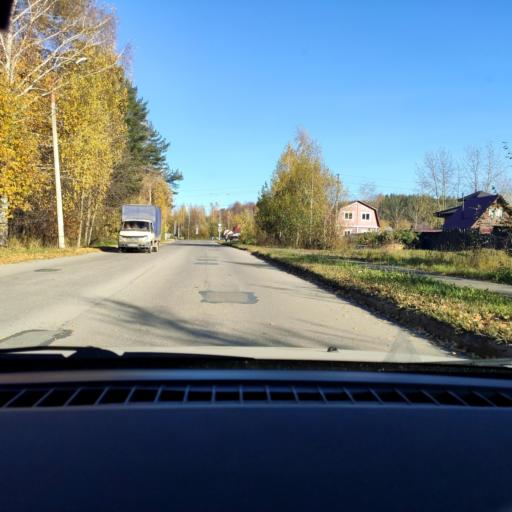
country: RU
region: Perm
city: Perm
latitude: 58.0795
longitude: 56.3705
